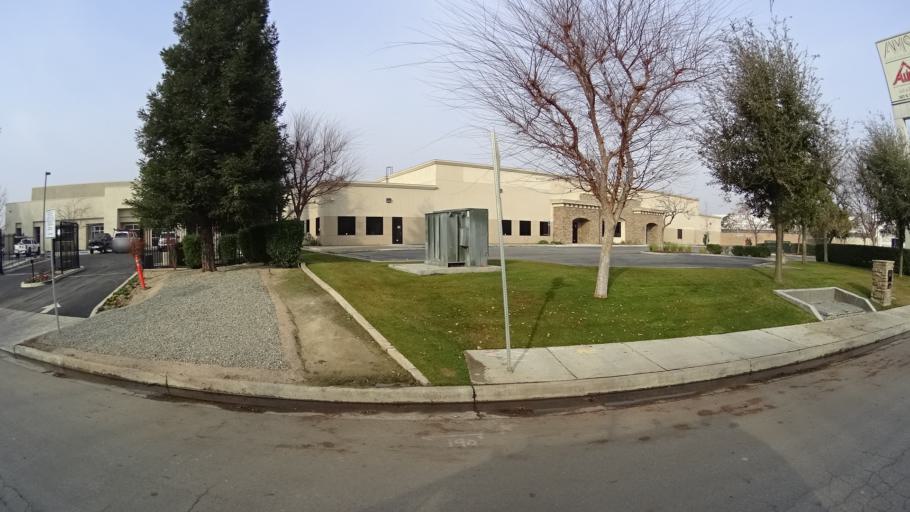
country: US
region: California
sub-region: Kern County
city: Bakersfield
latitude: 35.3909
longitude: -119.0370
